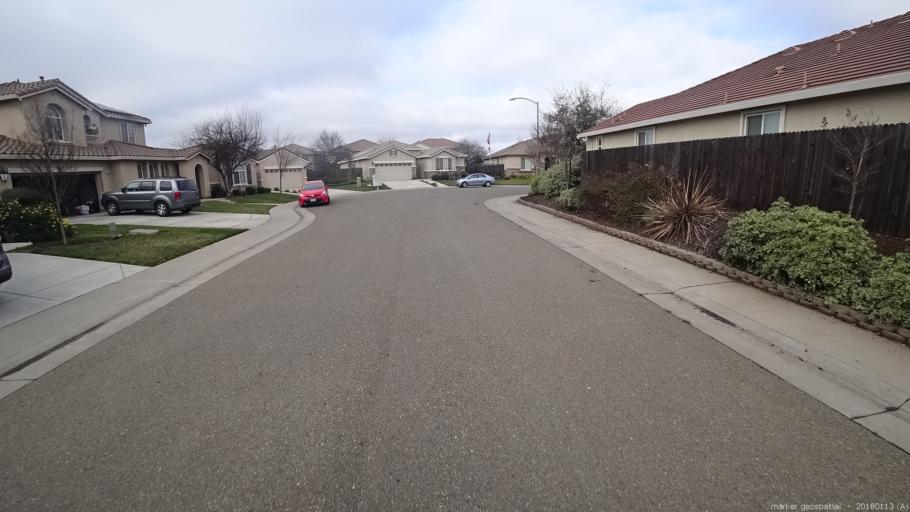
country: US
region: California
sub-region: Sacramento County
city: Gold River
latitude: 38.5563
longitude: -121.2115
